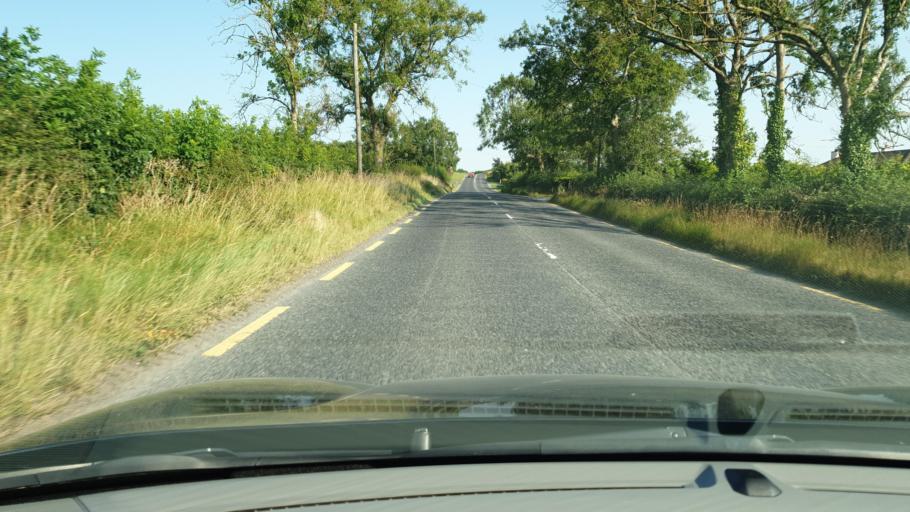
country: IE
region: Leinster
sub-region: An Mhi
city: Navan
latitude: 53.6392
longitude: -6.6126
